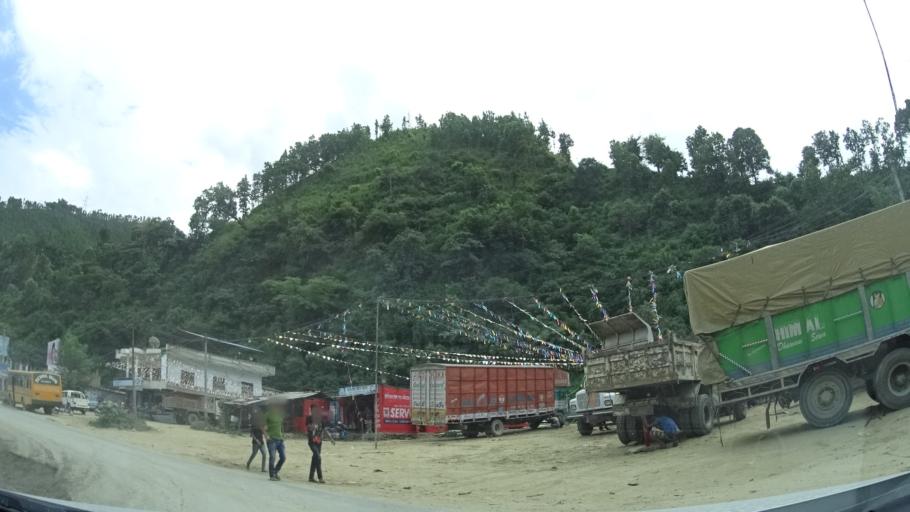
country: NP
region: Central Region
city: Kirtipur
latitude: 27.7955
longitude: 84.9985
